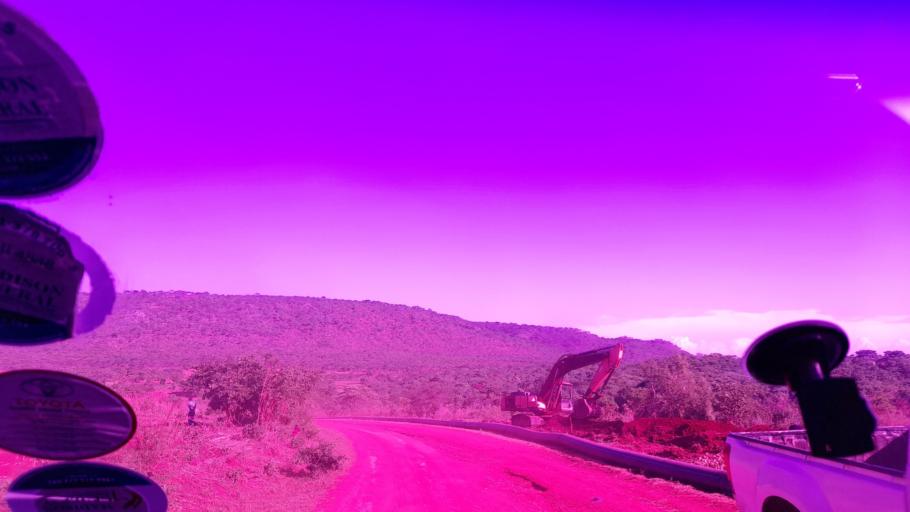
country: ZM
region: Northern
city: Mpika
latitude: -11.7326
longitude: 31.4837
